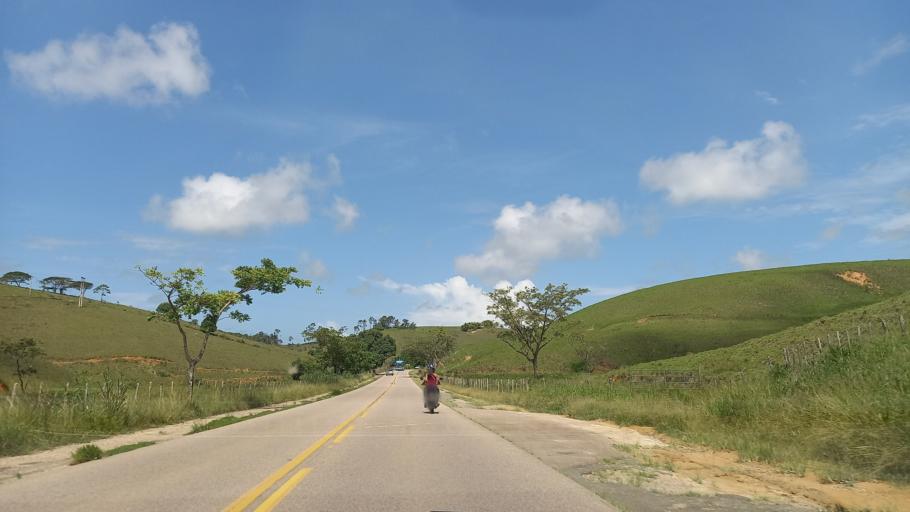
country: BR
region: Pernambuco
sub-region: Tamandare
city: Tamandare
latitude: -8.7437
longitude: -35.1732
